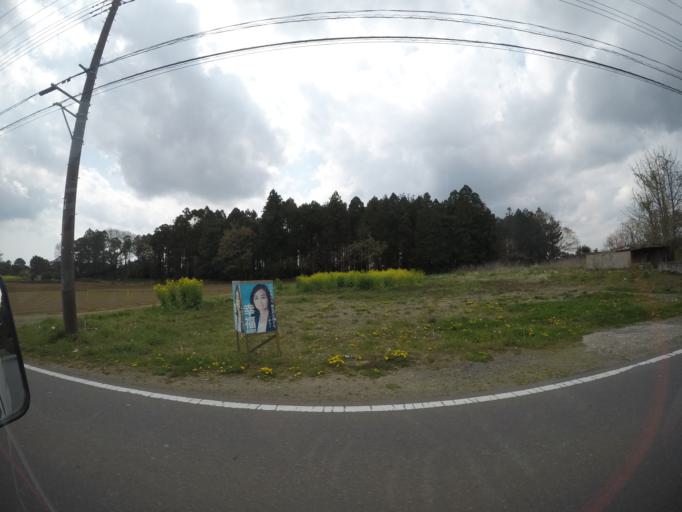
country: JP
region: Chiba
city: Sawara
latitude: 35.8441
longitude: 140.5231
